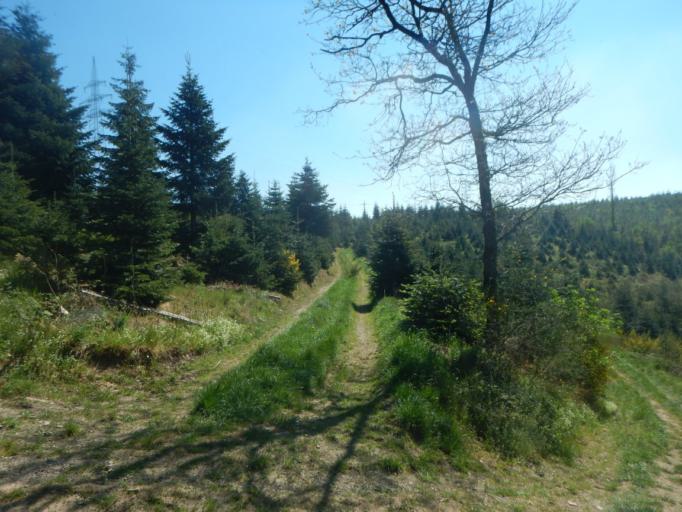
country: LU
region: Diekirch
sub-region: Canton de Diekirch
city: Bourscheid
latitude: 49.9145
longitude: 6.0964
